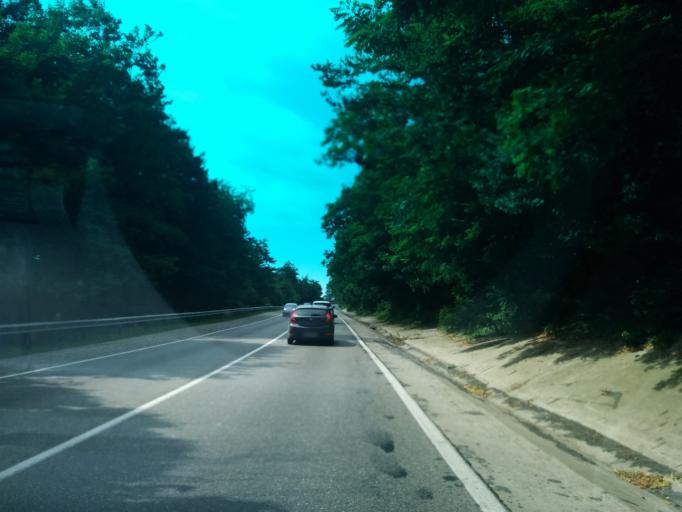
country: RU
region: Krasnodarskiy
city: Nebug
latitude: 44.1760
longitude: 38.9734
